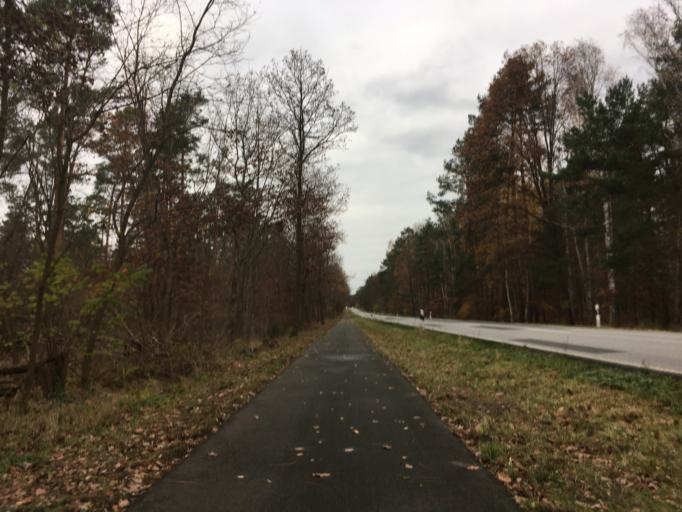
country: DE
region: Brandenburg
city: Mullrose
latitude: 52.2094
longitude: 14.4528
